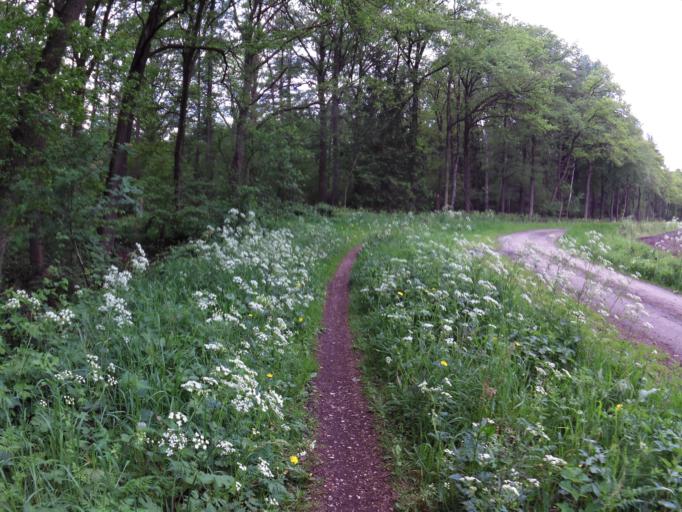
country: NL
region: North Brabant
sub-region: Gemeente Oirschot
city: Oirschot
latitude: 51.5423
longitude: 5.3352
